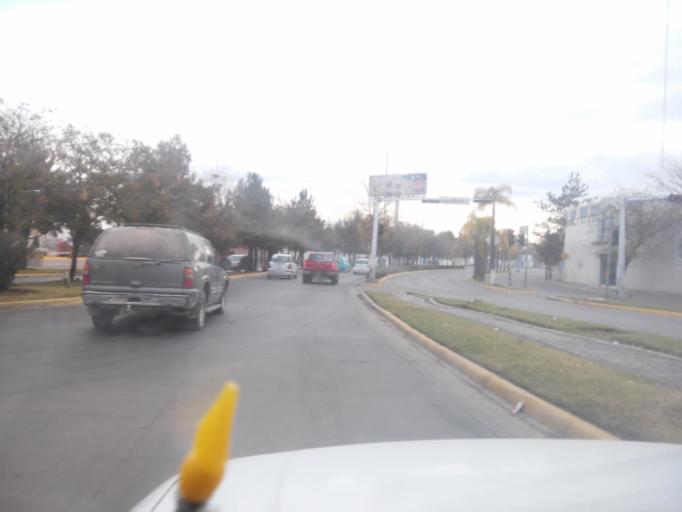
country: MX
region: Durango
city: Victoria de Durango
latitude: 24.0089
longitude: -104.6622
